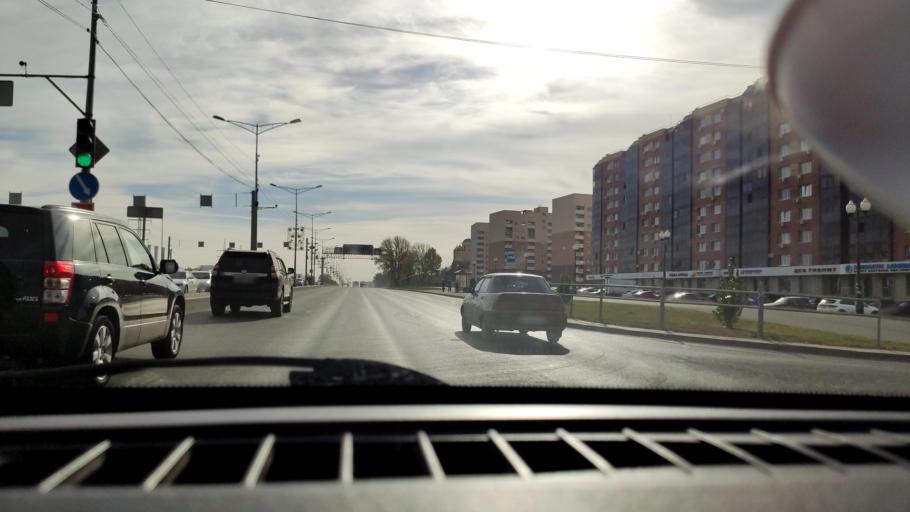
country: RU
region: Samara
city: Petra-Dubrava
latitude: 53.3081
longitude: 50.2915
